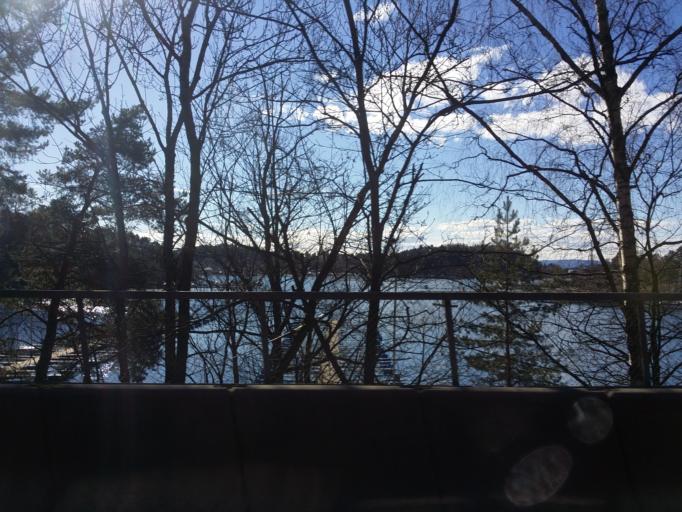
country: NO
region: Oslo
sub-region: Oslo
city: Oslo
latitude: 59.8750
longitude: 10.7779
